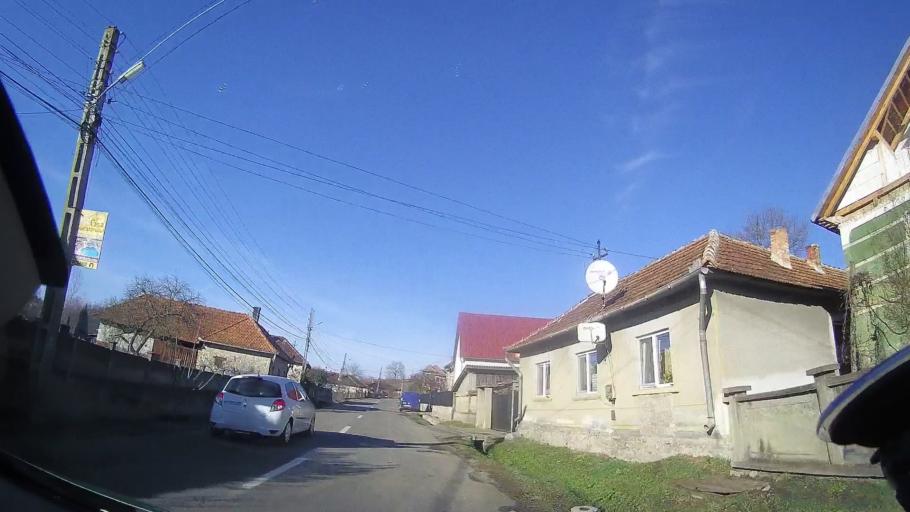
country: RO
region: Bihor
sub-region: Comuna Bratca
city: Beznea
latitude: 46.9537
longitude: 22.6113
